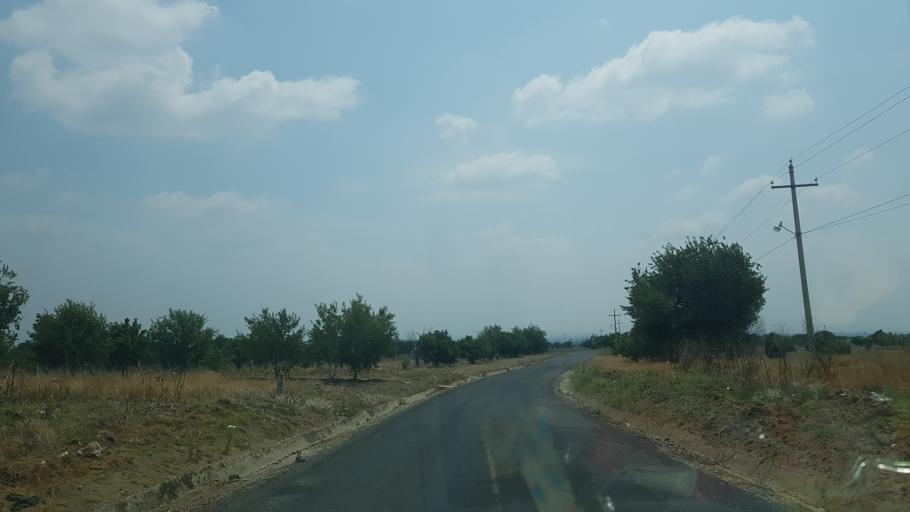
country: MX
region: Puebla
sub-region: Huejotzingo
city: San Juan Pancoac
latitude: 19.1377
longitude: -98.4249
